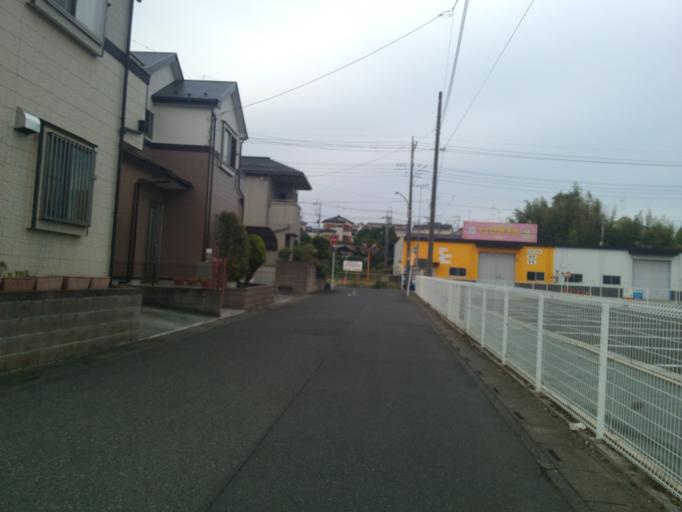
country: JP
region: Saitama
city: Fukiage-fujimi
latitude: 36.0432
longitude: 139.4100
